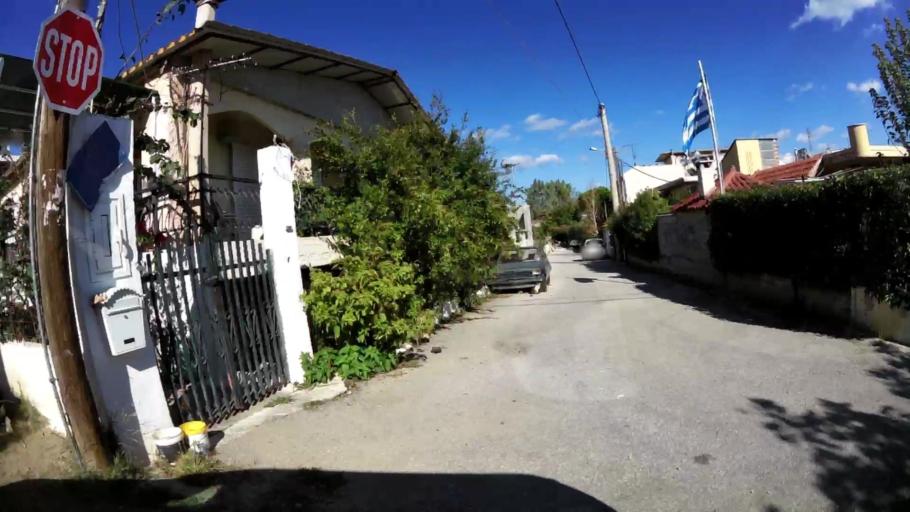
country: GR
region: Attica
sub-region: Nomarchia Anatolikis Attikis
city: Acharnes
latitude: 38.1059
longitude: 23.7216
